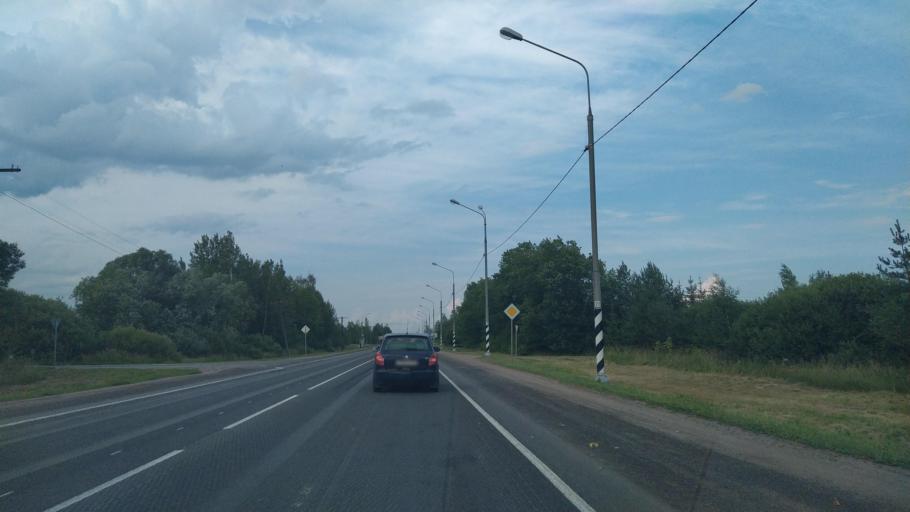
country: RU
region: Novgorod
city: Pankovka
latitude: 58.3844
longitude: 31.0194
